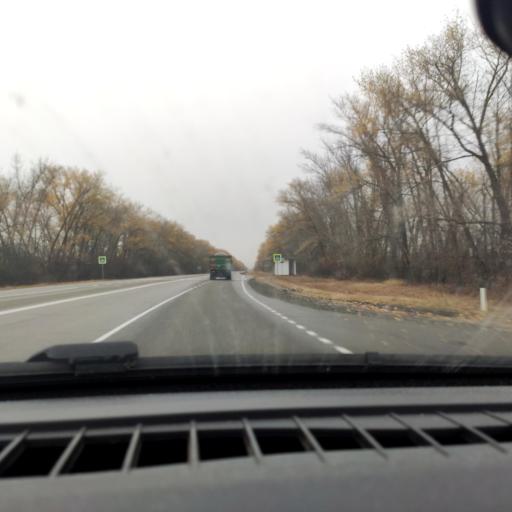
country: RU
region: Voronezj
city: Ostrogozhsk
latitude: 50.9774
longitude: 38.9936
